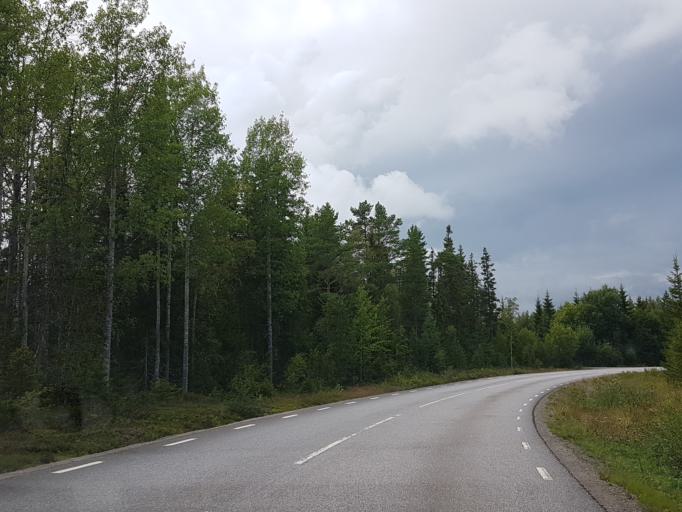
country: SE
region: Vaesterbotten
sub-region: Umea Kommun
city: Holmsund
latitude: 63.7955
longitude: 20.3689
